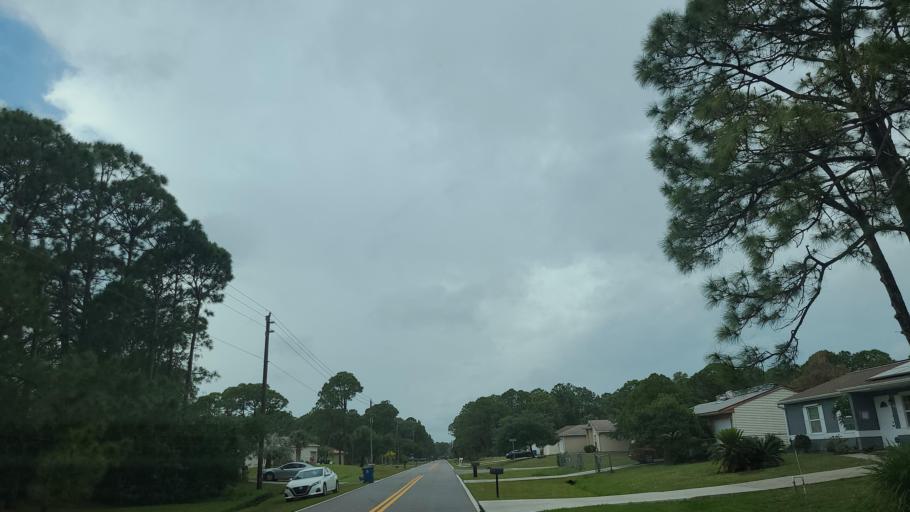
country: US
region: Florida
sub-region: Brevard County
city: Grant-Valkaria
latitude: 27.9393
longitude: -80.6264
